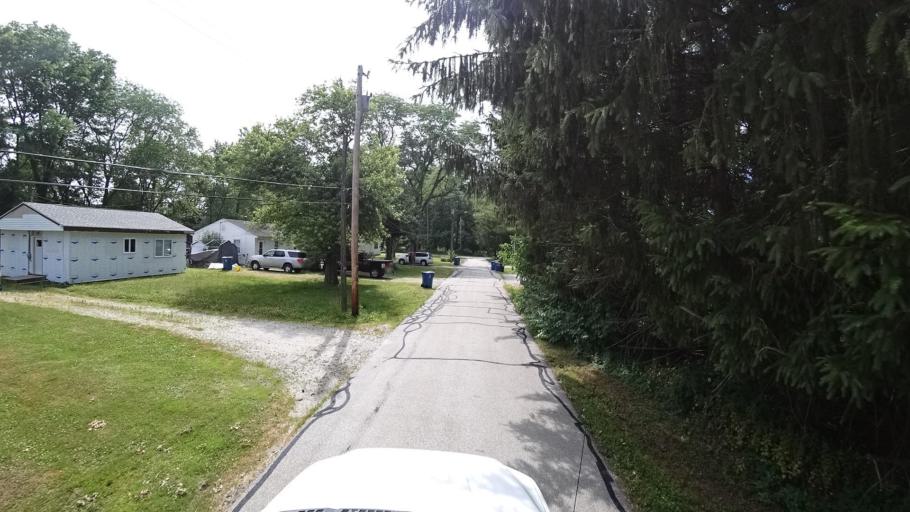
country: US
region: Indiana
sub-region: Porter County
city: Porter
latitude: 41.6087
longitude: -87.0830
